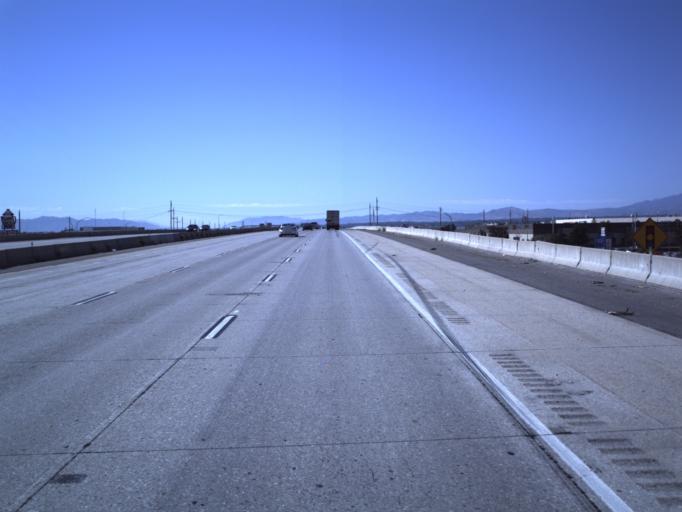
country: US
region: Utah
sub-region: Salt Lake County
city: Salt Lake City
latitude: 40.7429
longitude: -111.9493
